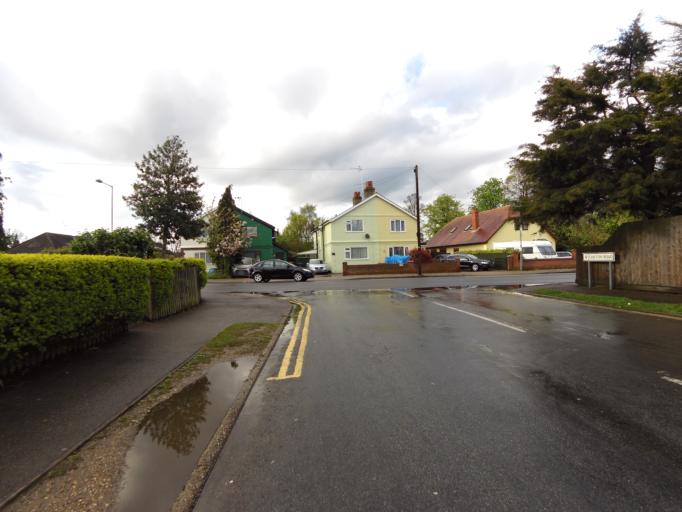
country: GB
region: England
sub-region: Suffolk
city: Ipswich
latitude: 52.0516
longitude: 1.1955
